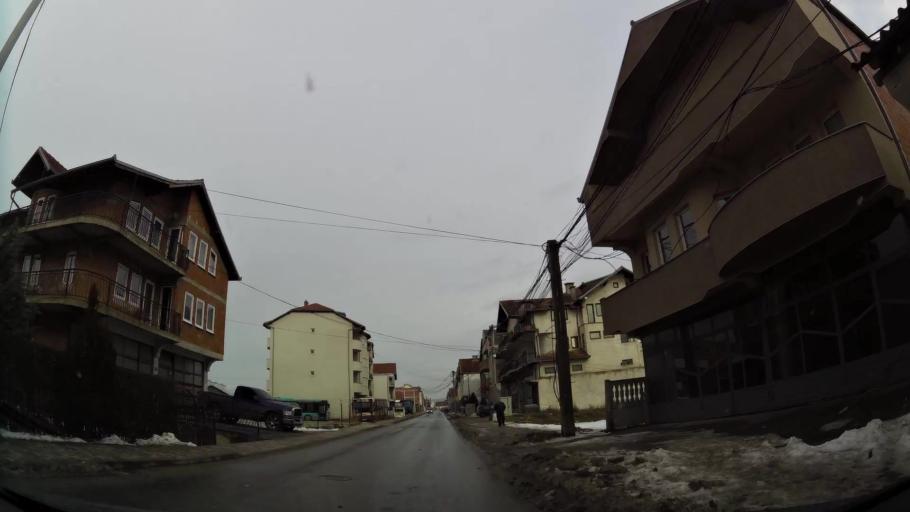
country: XK
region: Pristina
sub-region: Komuna e Prishtines
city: Pristina
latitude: 42.6879
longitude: 21.1596
